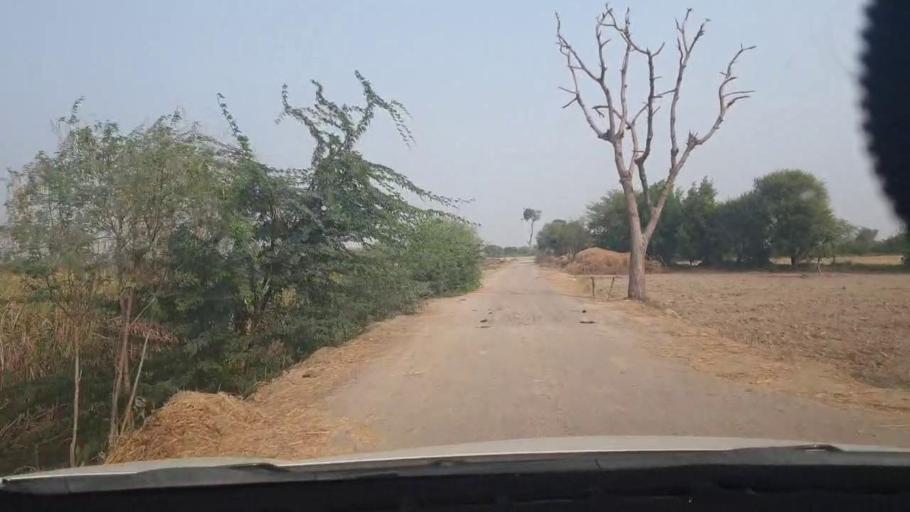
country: PK
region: Sindh
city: Tando Muhammad Khan
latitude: 24.9721
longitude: 68.4915
